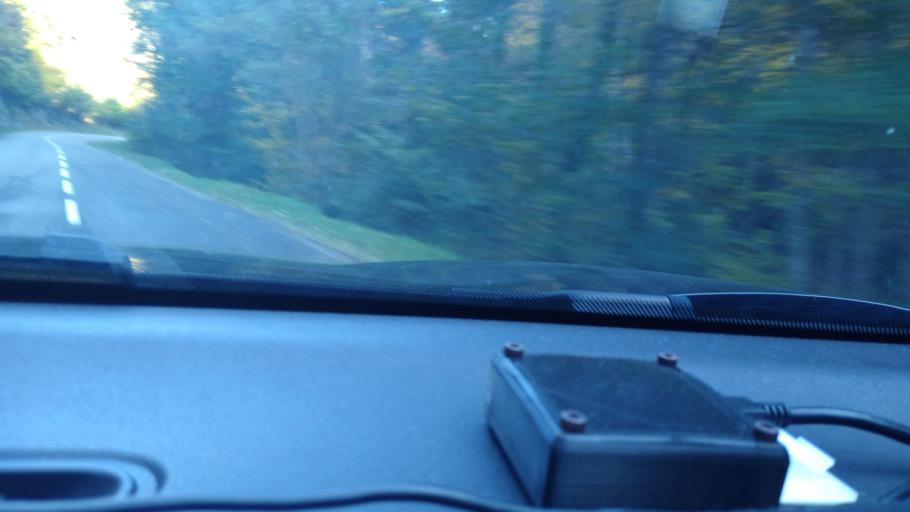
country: FR
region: Languedoc-Roussillon
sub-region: Departement de l'Aude
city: Quillan
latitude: 42.7332
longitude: 2.0975
